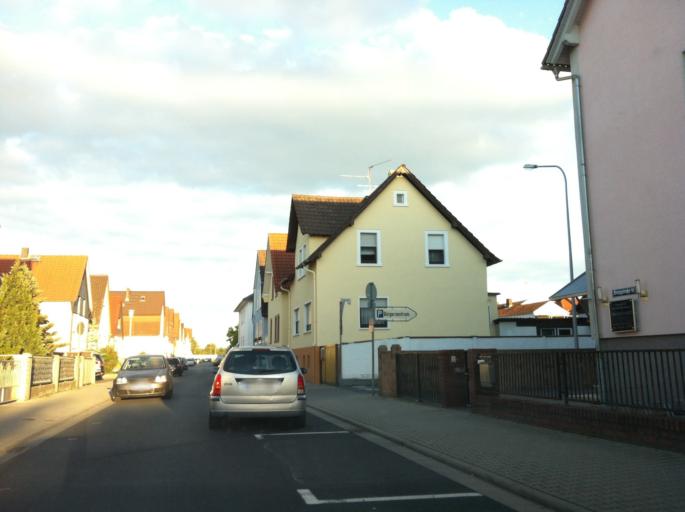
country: DE
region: Hesse
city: Weiterstadt
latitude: 49.9080
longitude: 8.5854
